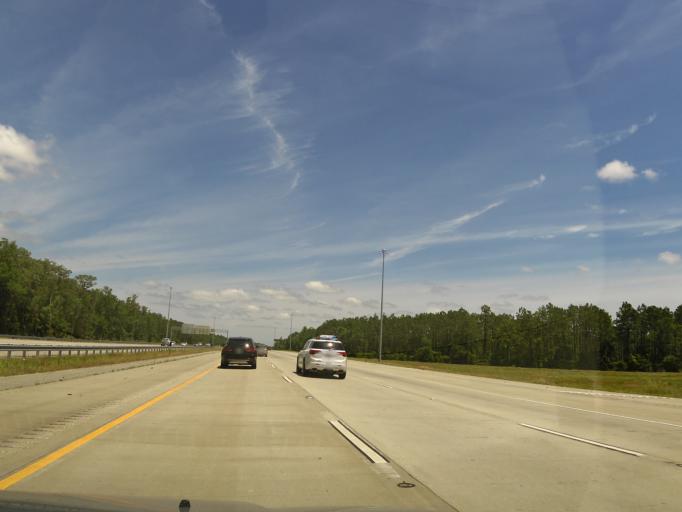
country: US
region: Georgia
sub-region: McIntosh County
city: Darien
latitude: 31.3082
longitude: -81.4791
